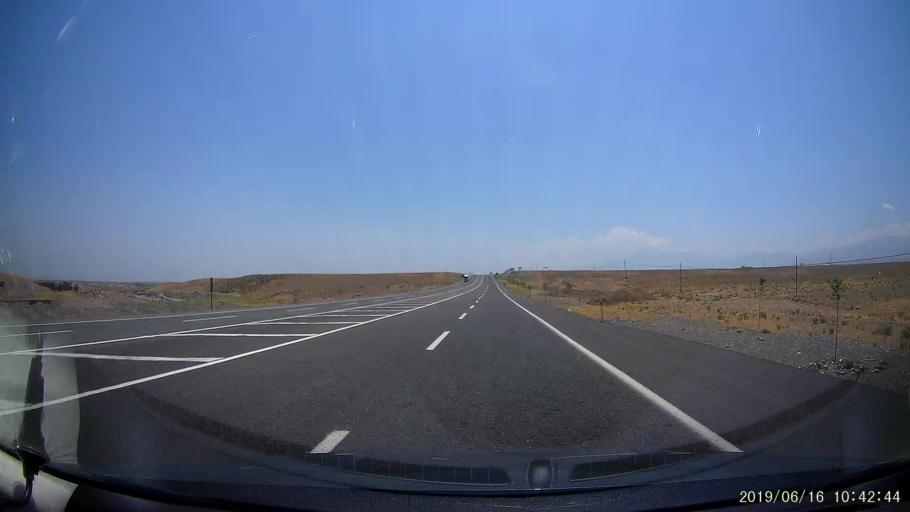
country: AM
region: Armavir
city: Shenavan
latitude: 40.0399
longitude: 43.8133
